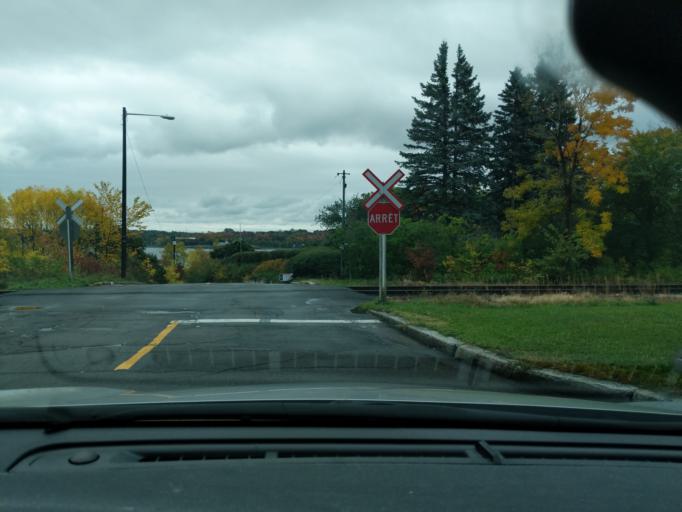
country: CA
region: Quebec
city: Quebec
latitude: 46.7627
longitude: -71.2667
